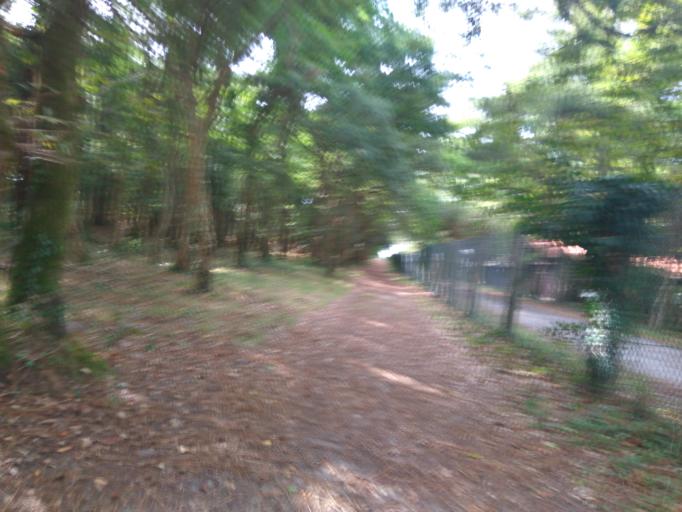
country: FR
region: Aquitaine
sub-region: Departement des Landes
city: Capbreton
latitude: 43.6284
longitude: -1.4447
